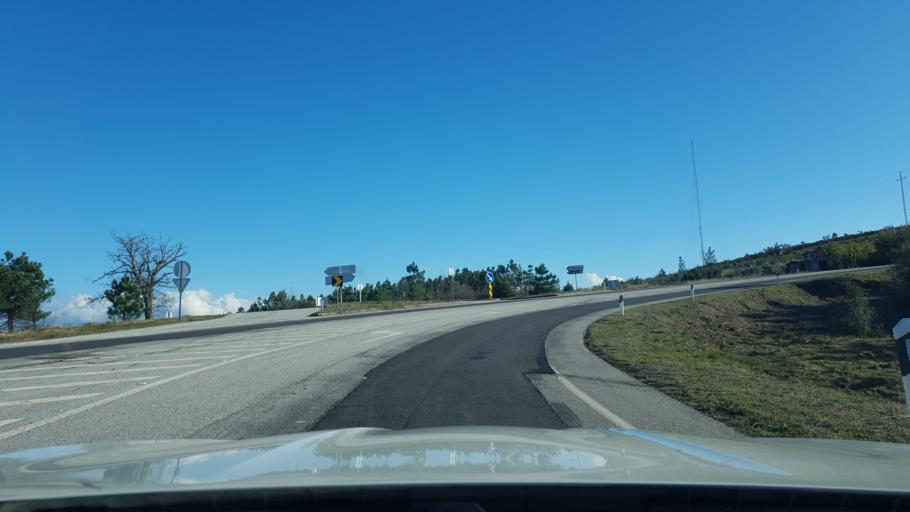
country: PT
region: Braganca
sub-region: Freixo de Espada A Cinta
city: Freixo de Espada a Cinta
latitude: 41.1547
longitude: -6.7977
